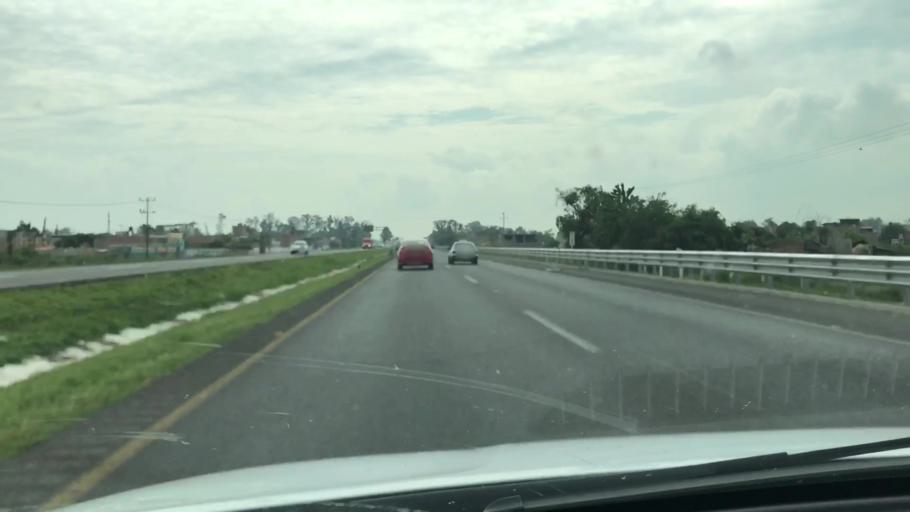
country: MX
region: Guanajuato
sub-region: Irapuato
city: Las Huertas Tercera Seccion
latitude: 20.6496
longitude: -101.3693
